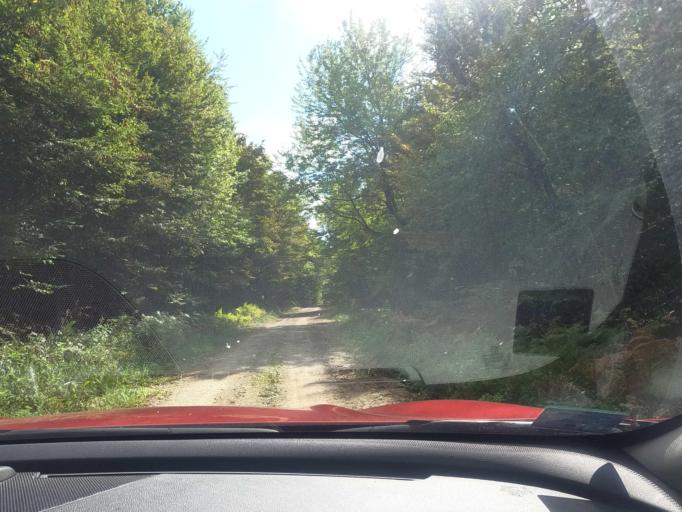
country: BA
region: Federation of Bosnia and Herzegovina
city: Velika Kladusa
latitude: 45.2562
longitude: 15.7899
